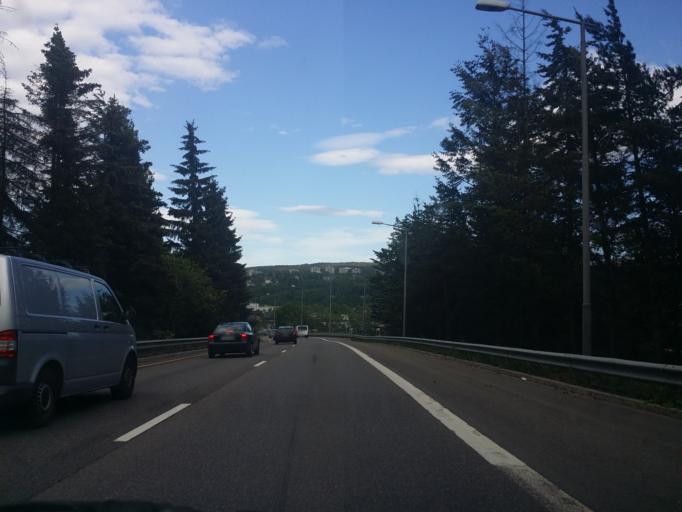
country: NO
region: Oslo
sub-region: Oslo
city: Oslo
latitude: 59.9228
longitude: 10.8250
